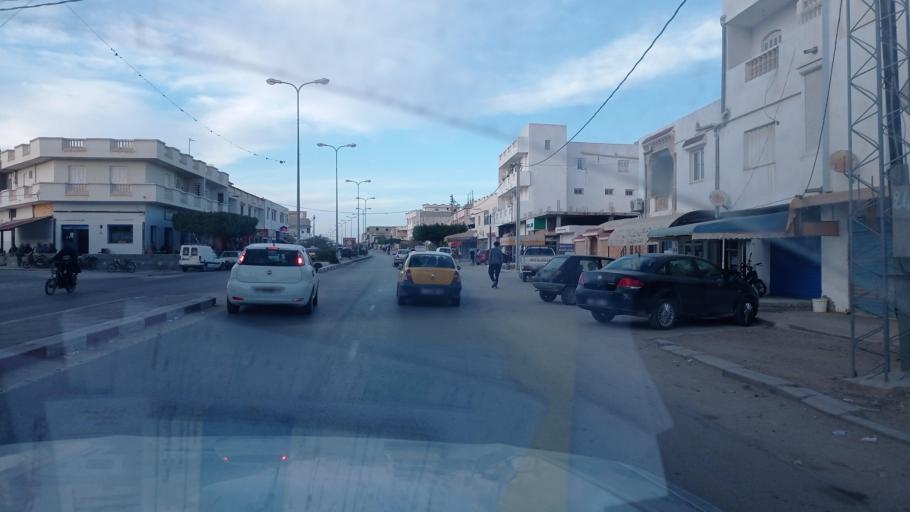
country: TN
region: Qabis
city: Gabes
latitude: 33.8446
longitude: 10.1135
